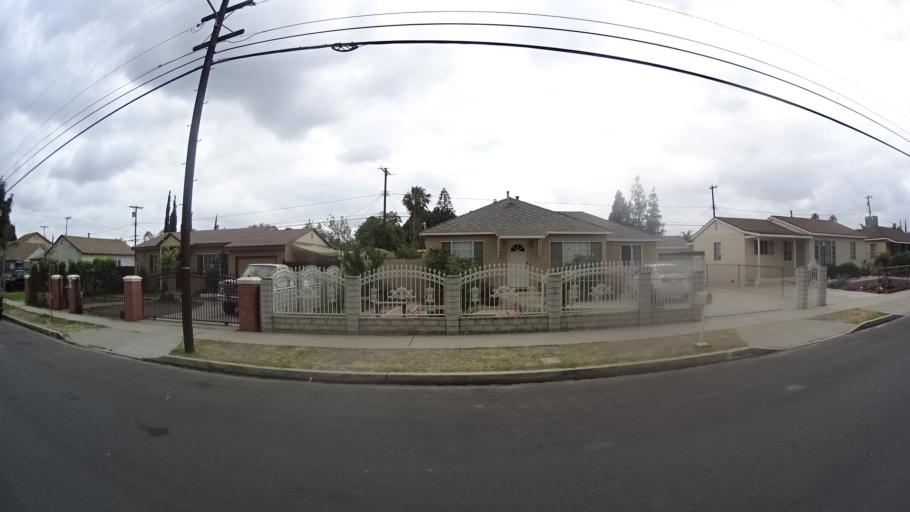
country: US
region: California
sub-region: Los Angeles County
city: San Fernando
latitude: 34.2601
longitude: -118.4393
